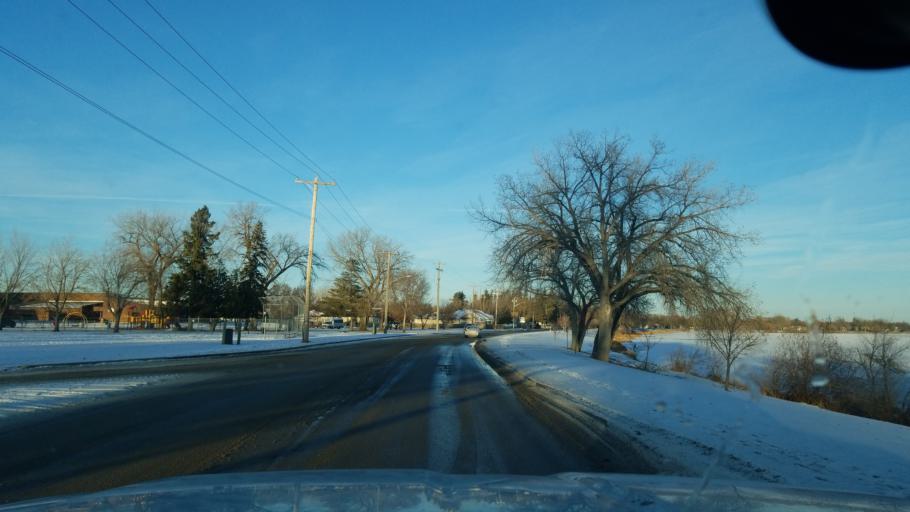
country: CA
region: Manitoba
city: Portage la Prairie
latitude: 49.9650
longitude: -98.3205
